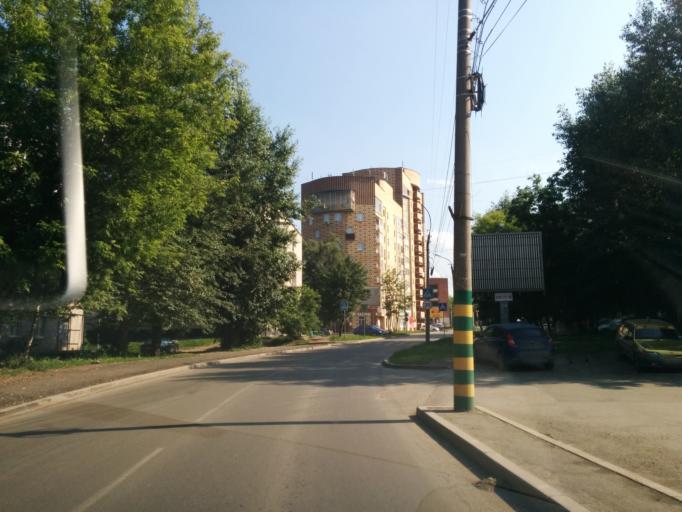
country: RU
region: Perm
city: Perm
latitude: 57.9987
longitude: 56.2085
